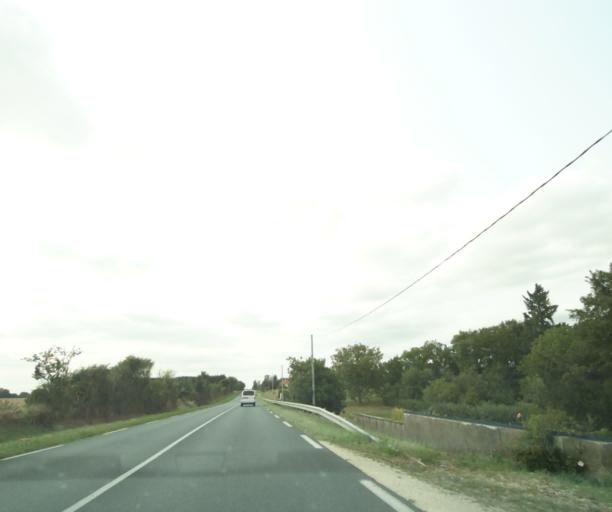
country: FR
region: Centre
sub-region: Departement de l'Indre
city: Chatillon-sur-Indre
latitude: 47.0016
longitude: 1.1460
